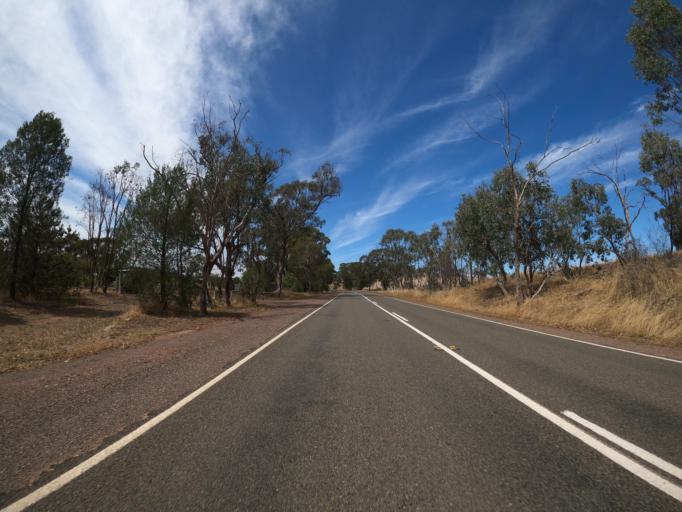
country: AU
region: Victoria
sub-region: Benalla
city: Benalla
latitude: -36.3217
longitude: 145.9586
